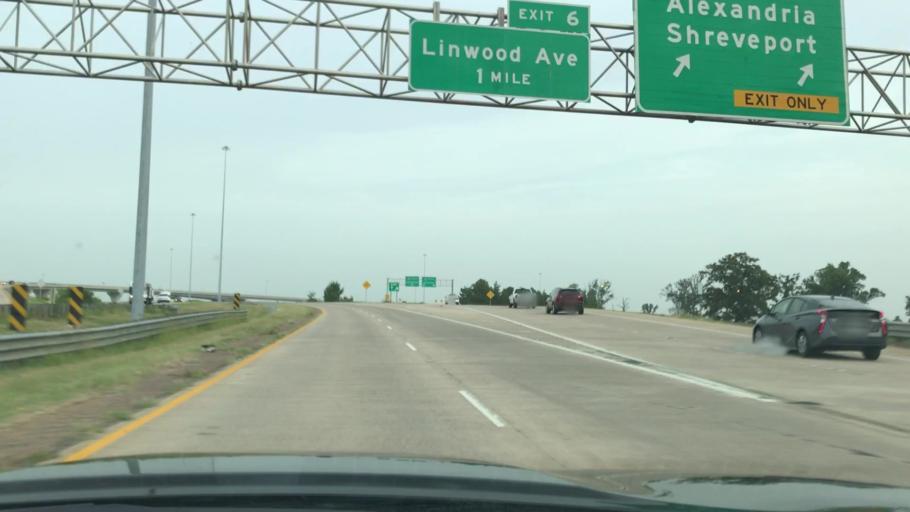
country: US
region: Louisiana
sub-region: Bossier Parish
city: Bossier City
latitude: 32.4180
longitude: -93.7428
